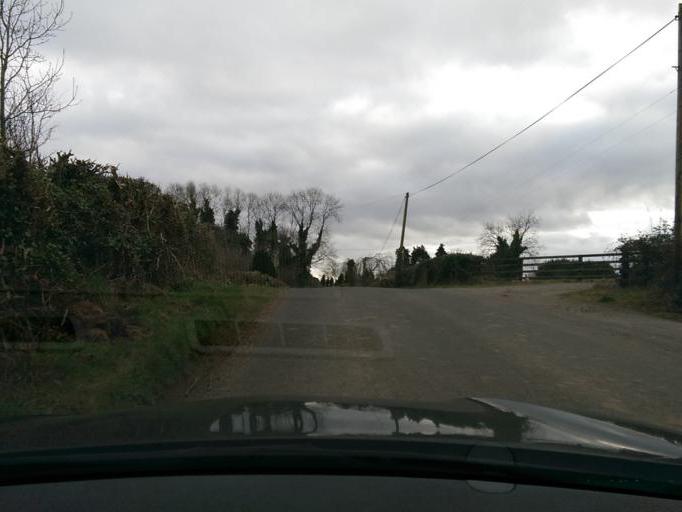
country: IE
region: Leinster
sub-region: An Iarmhi
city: Moate
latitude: 53.3847
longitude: -7.8240
